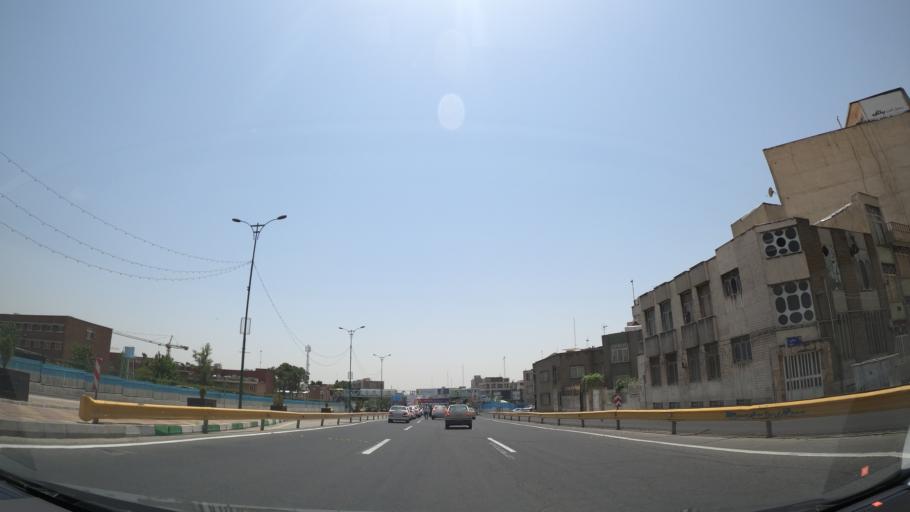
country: IR
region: Tehran
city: Tehran
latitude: 35.7077
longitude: 51.3776
